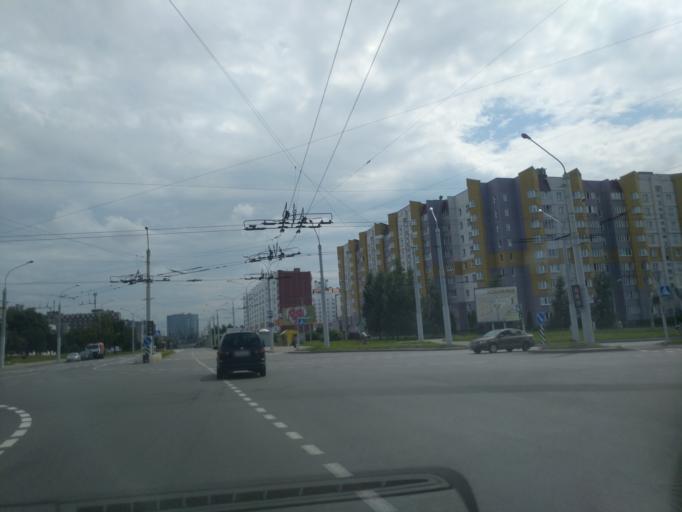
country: BY
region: Minsk
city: Novoye Medvezhino
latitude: 53.8812
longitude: 27.4855
